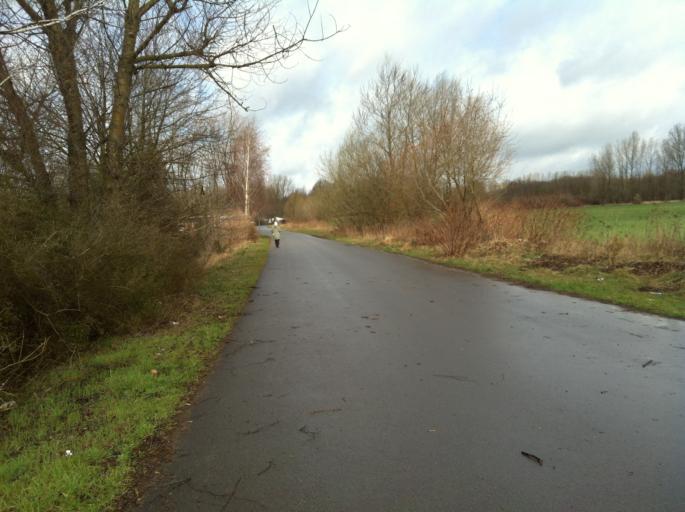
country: DE
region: Berlin
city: Karow
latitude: 52.6218
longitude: 13.4759
